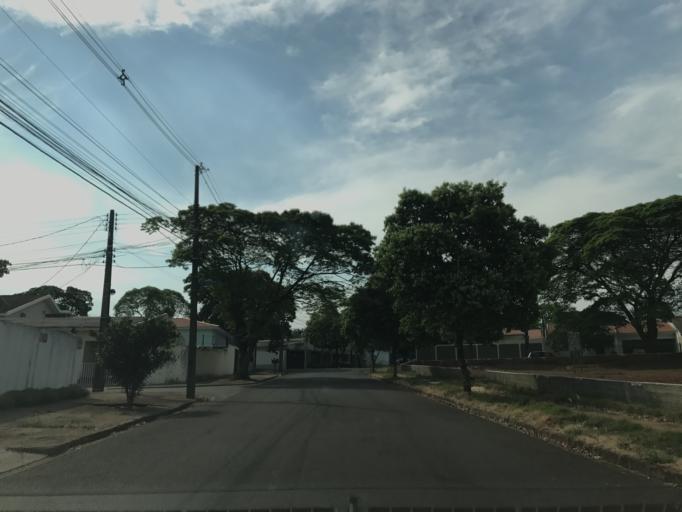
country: BR
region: Parana
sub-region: Maringa
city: Maringa
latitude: -23.4367
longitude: -51.9539
